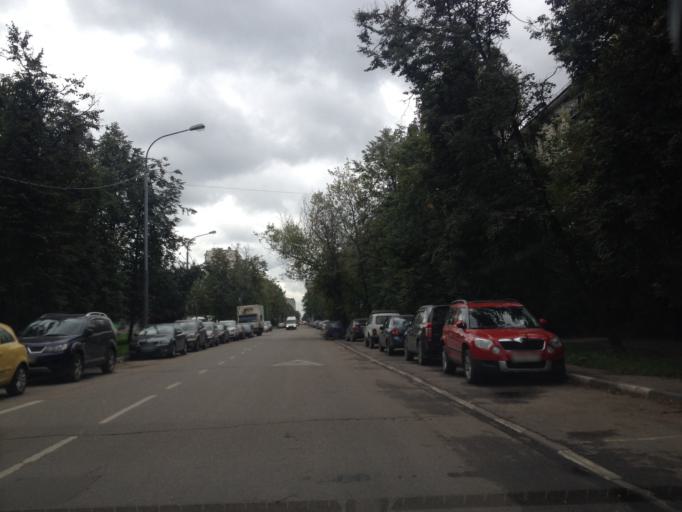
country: RU
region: Moscow
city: Gol'yanovo
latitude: 55.8098
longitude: 37.8048
